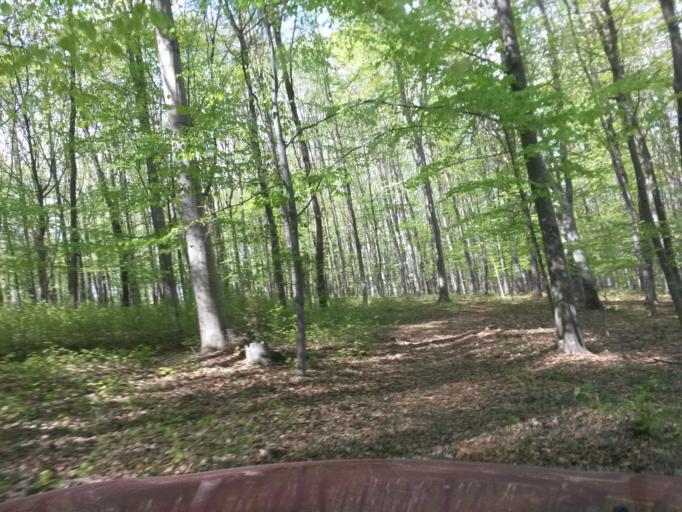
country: SK
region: Presovsky
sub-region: Okres Presov
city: Presov
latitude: 48.9437
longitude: 21.1230
